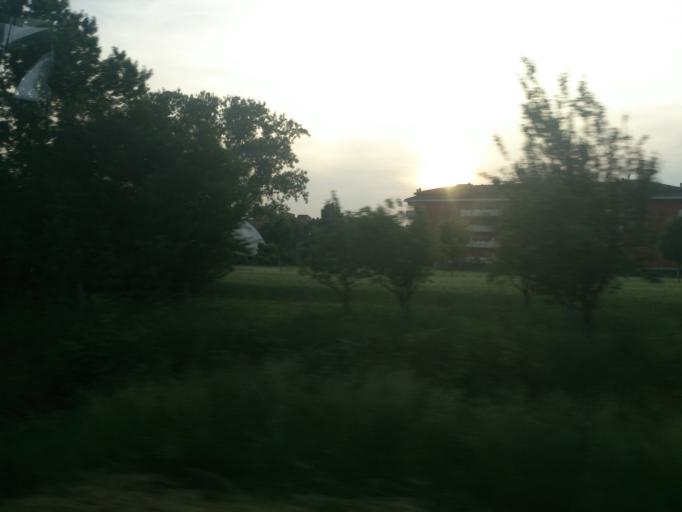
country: IT
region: Lombardy
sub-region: Provincia di Bergamo
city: Azzano San Paolo
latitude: 45.6715
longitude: 9.6681
